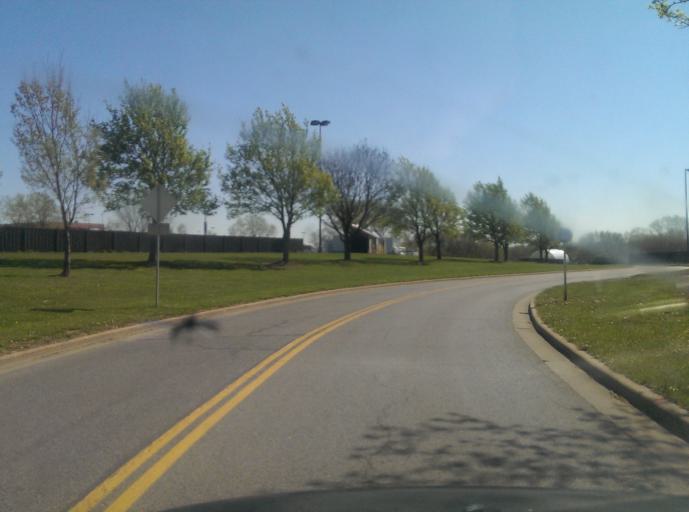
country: US
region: Kansas
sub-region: Johnson County
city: Lenexa
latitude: 38.9207
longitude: -94.7312
